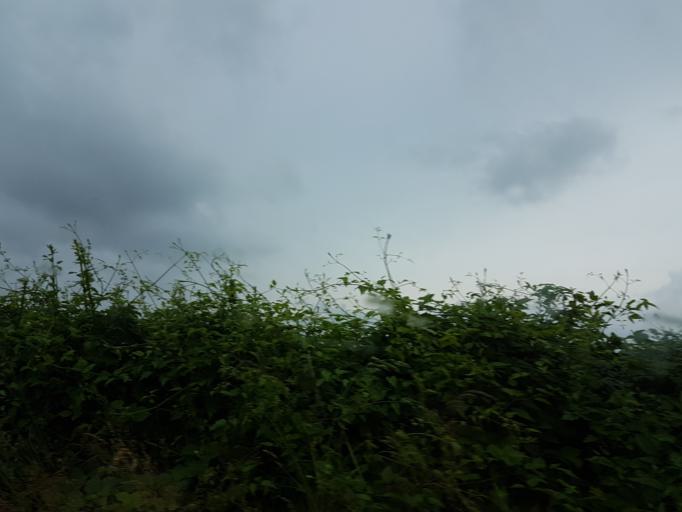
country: FR
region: Bourgogne
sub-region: Departement de la Nievre
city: Corbigny
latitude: 47.2153
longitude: 3.7127
